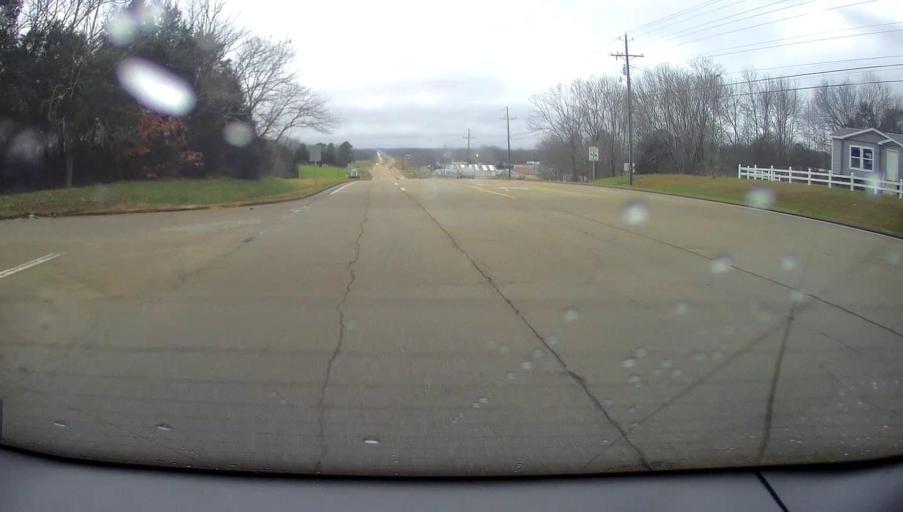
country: US
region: Mississippi
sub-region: Alcorn County
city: Corinth
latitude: 34.9308
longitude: -88.5640
